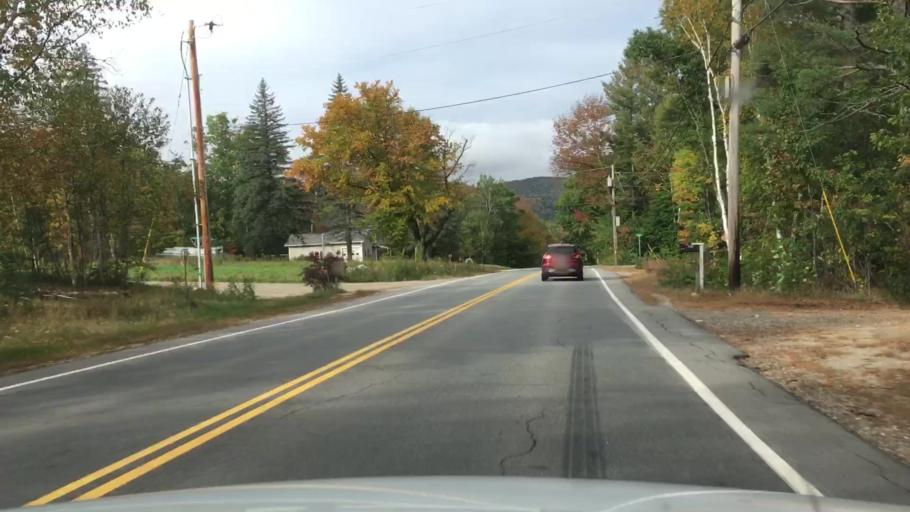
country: US
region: New Hampshire
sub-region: Coos County
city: Gorham
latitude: 44.3863
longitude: -71.1447
